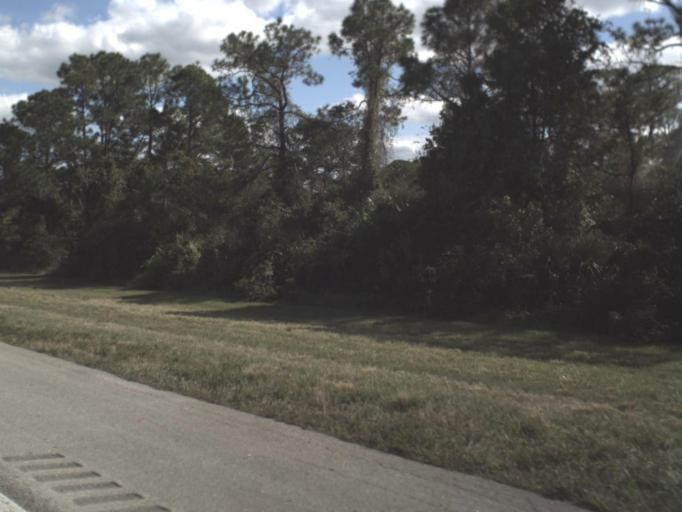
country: US
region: Florida
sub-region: Indian River County
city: Fellsmere
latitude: 27.5639
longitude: -80.7835
